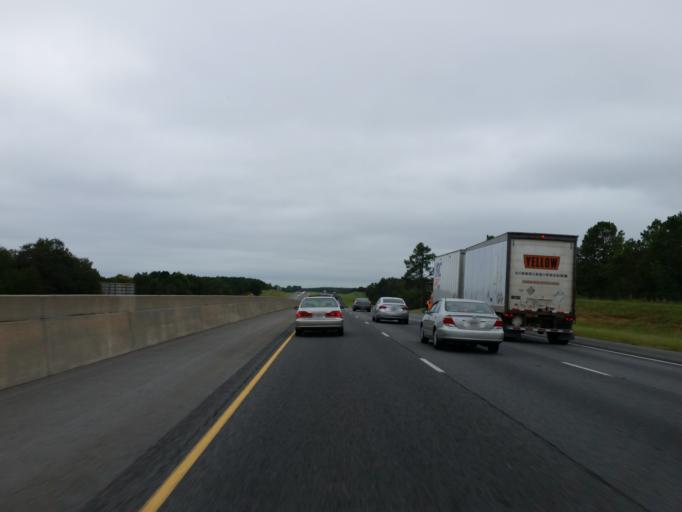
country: US
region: Georgia
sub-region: Turner County
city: Ashburn
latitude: 31.8245
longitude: -83.7111
